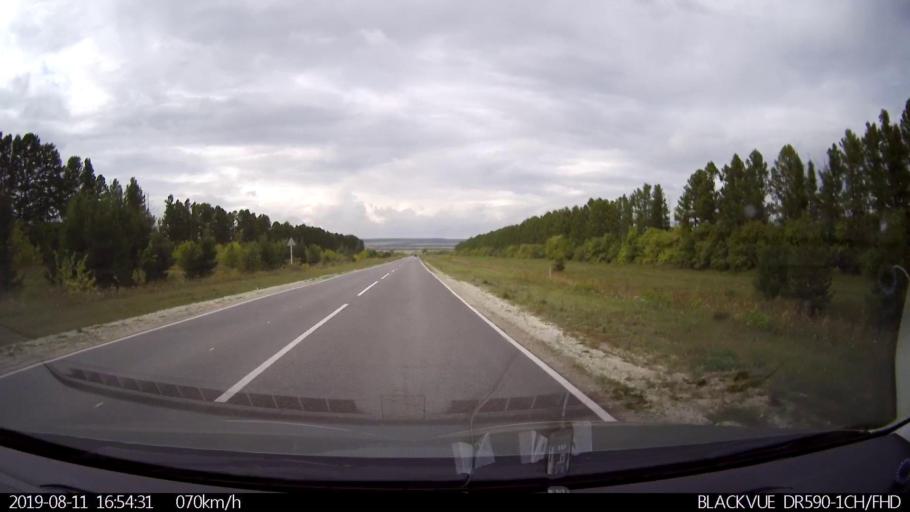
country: RU
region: Ulyanovsk
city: Mayna
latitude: 54.2736
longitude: 47.6662
